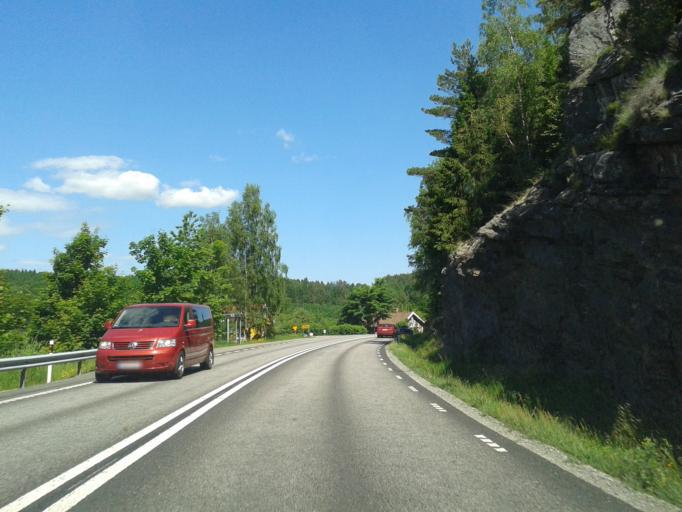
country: SE
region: Vaestra Goetaland
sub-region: Orust
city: Henan
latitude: 58.3315
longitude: 11.6865
